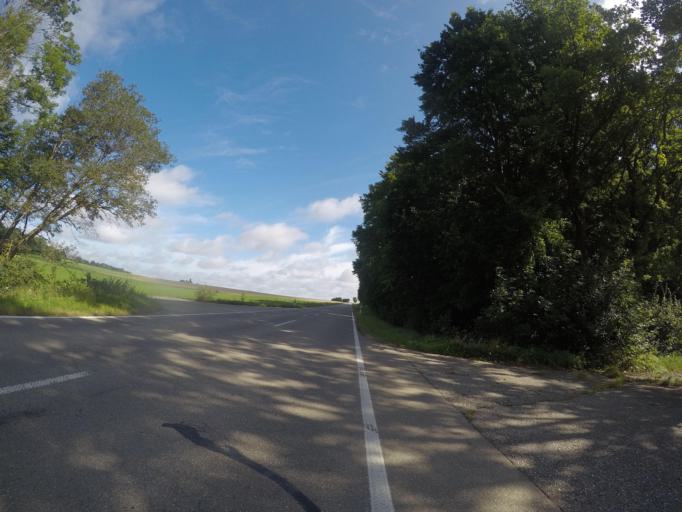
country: DE
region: Baden-Wuerttemberg
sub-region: Tuebingen Region
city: Laichingen
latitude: 48.4160
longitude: 9.6507
